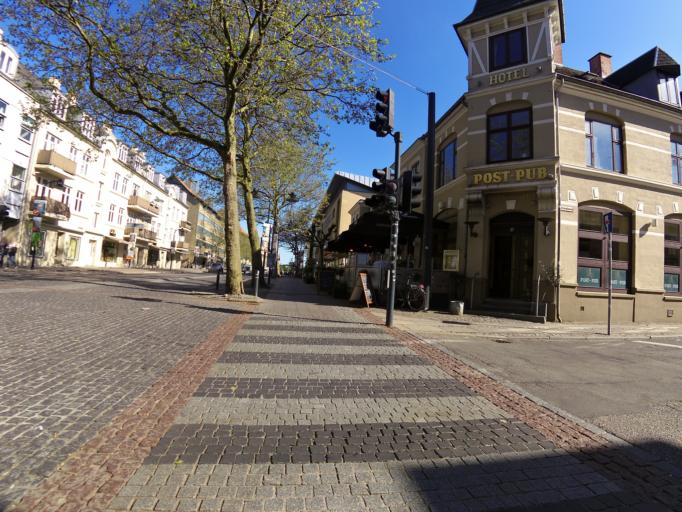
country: DK
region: Capital Region
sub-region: Lyngby-Tarbaek Kommune
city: Kongens Lyngby
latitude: 55.7691
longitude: 12.5053
